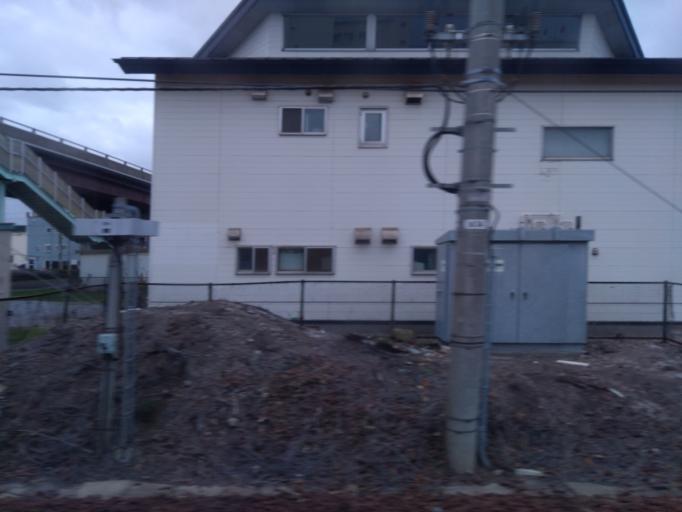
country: JP
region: Hokkaido
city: Hakodate
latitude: 41.7808
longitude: 140.7291
